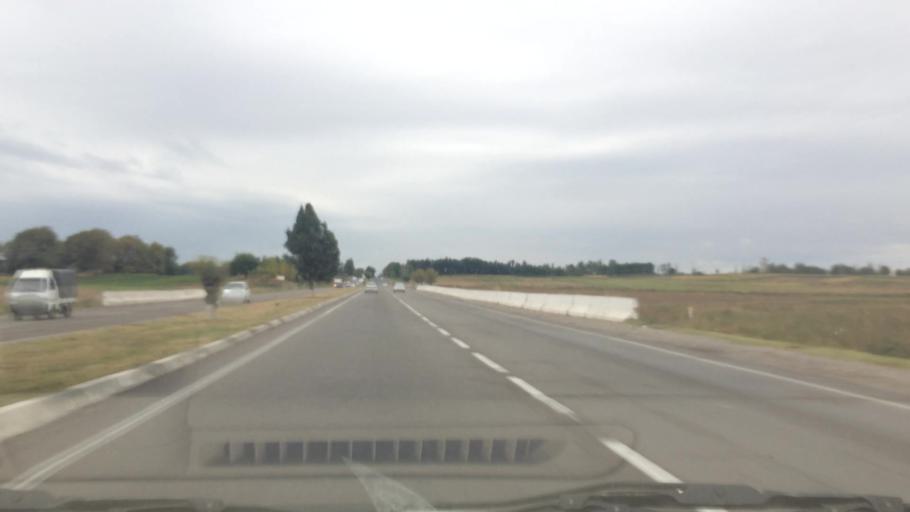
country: UZ
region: Toshkent
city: Amir Timur
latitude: 41.0805
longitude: 68.9380
